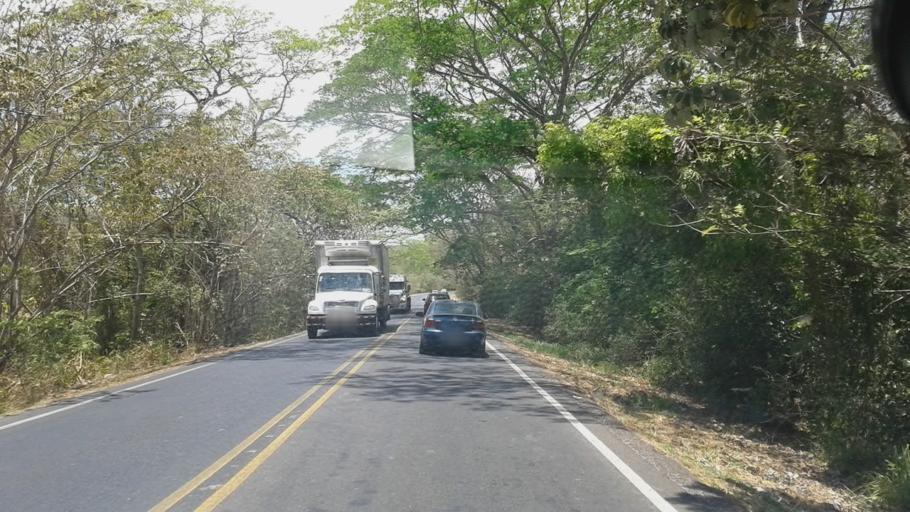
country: CR
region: Puntarenas
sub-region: Canton Central de Puntarenas
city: Puntarenas
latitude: 10.0882
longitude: -84.8481
